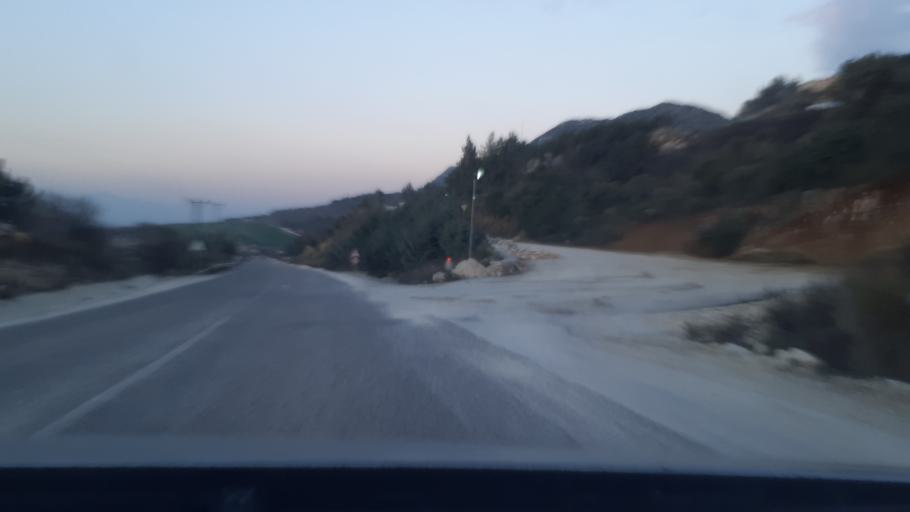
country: TR
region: Hatay
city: Dursunlu
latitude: 36.1750
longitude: 36.1875
